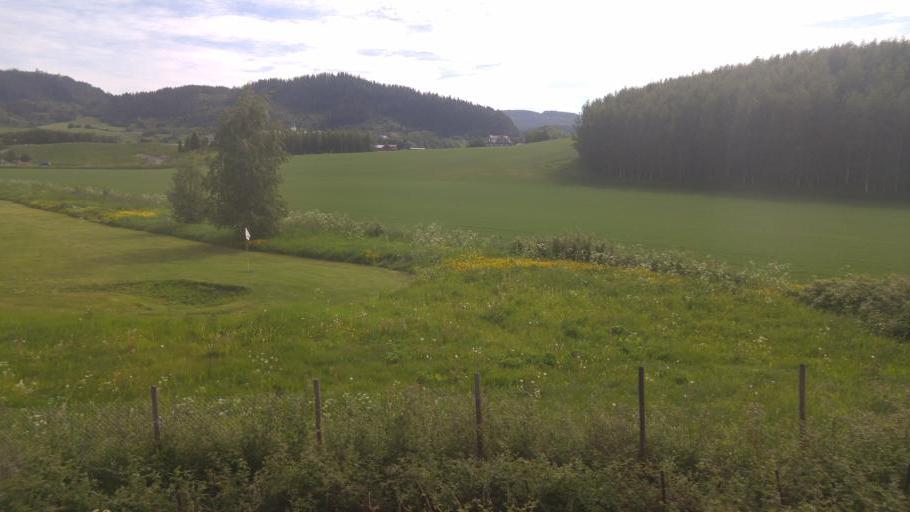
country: NO
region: Sor-Trondelag
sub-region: Melhus
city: Lundamo
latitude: 63.1945
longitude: 10.2973
